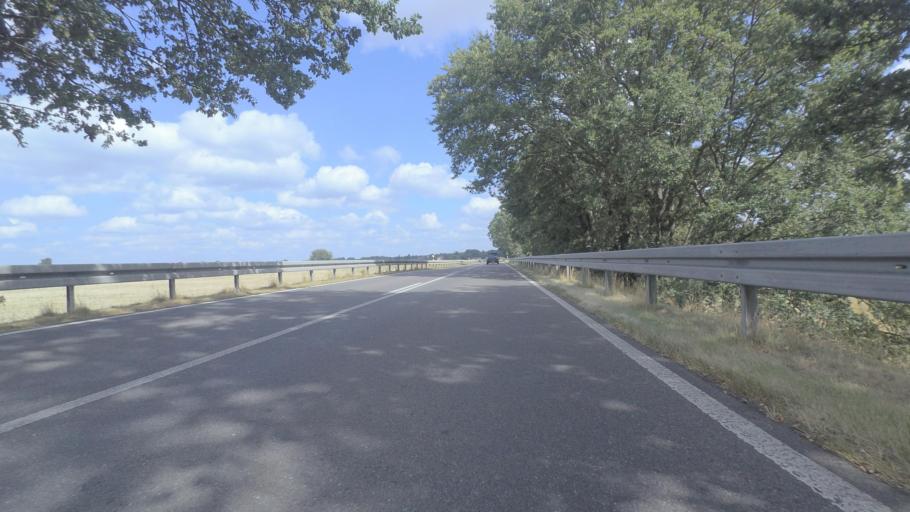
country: DE
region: Brandenburg
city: Walsleben
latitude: 53.0023
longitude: 12.6475
